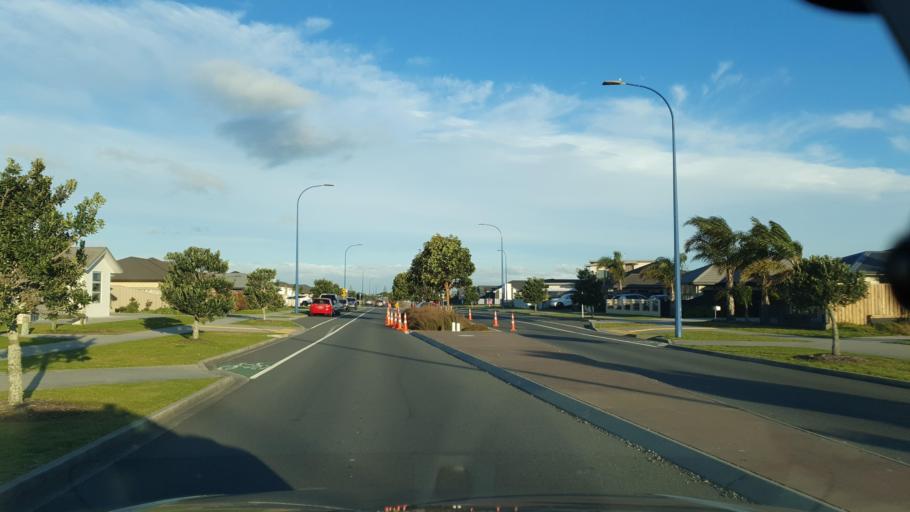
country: NZ
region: Bay of Plenty
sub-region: Western Bay of Plenty District
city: Maketu
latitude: -37.7223
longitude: 176.3353
